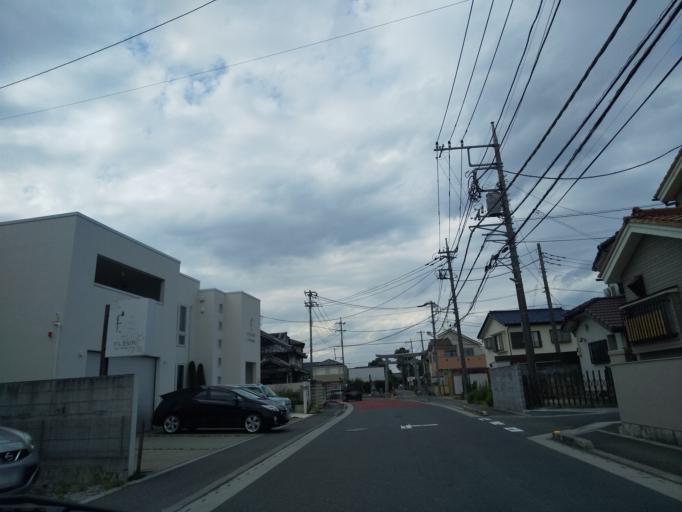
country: JP
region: Chiba
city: Noda
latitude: 35.9899
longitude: 139.8133
